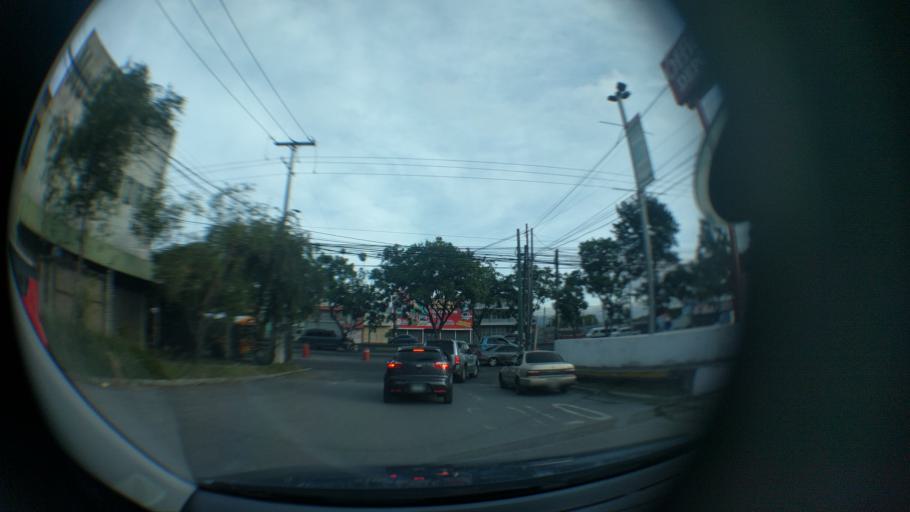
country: GT
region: Guatemala
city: Villa Nueva
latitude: 14.5832
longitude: -90.5655
